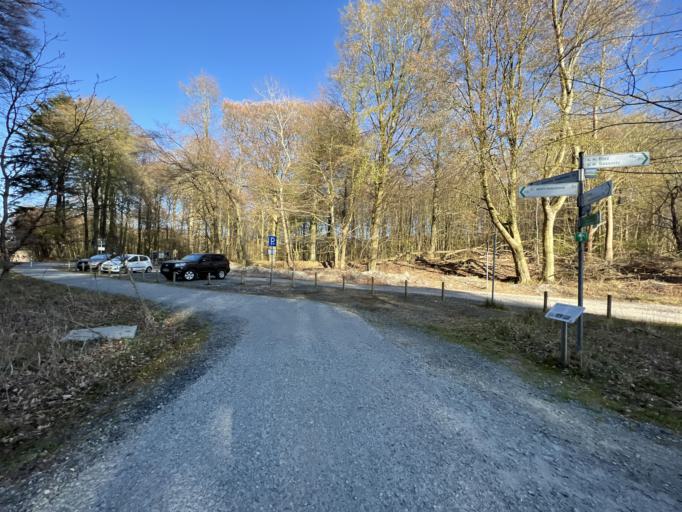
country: DE
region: Mecklenburg-Vorpommern
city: Sassnitz
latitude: 54.5299
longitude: 13.6420
